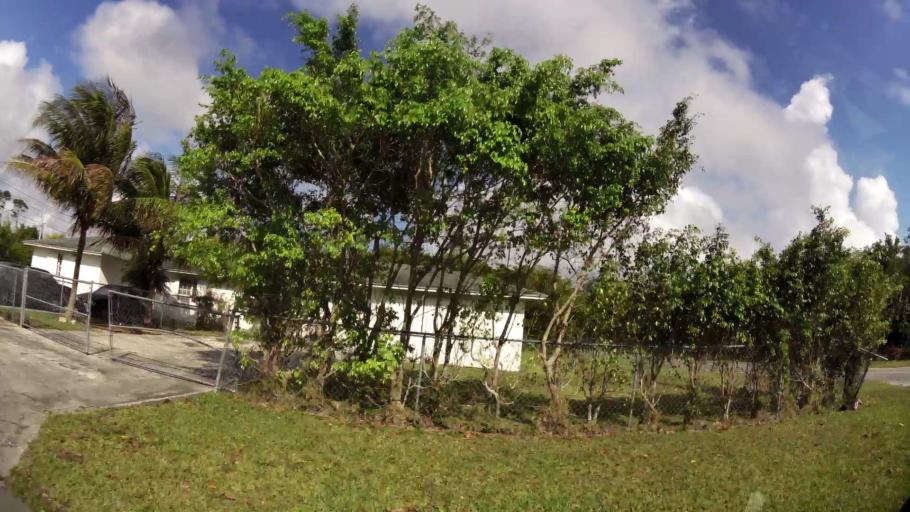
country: BS
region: Freeport
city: Lucaya
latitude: 26.5235
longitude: -78.6763
